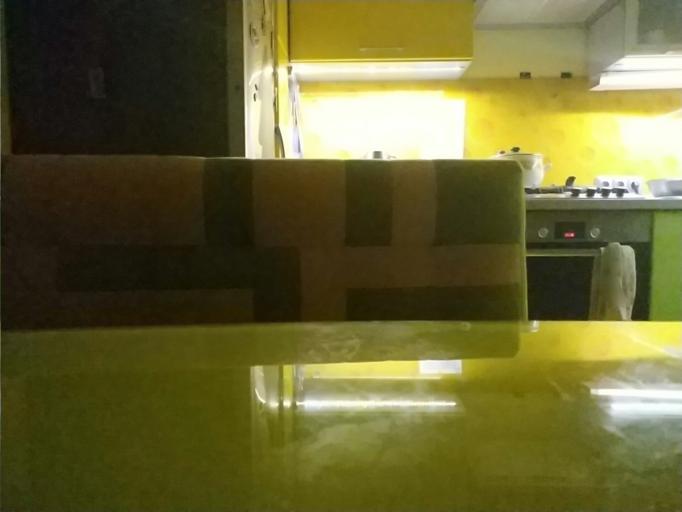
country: RU
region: Republic of Karelia
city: Kalevala
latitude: 65.2804
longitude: 30.7105
